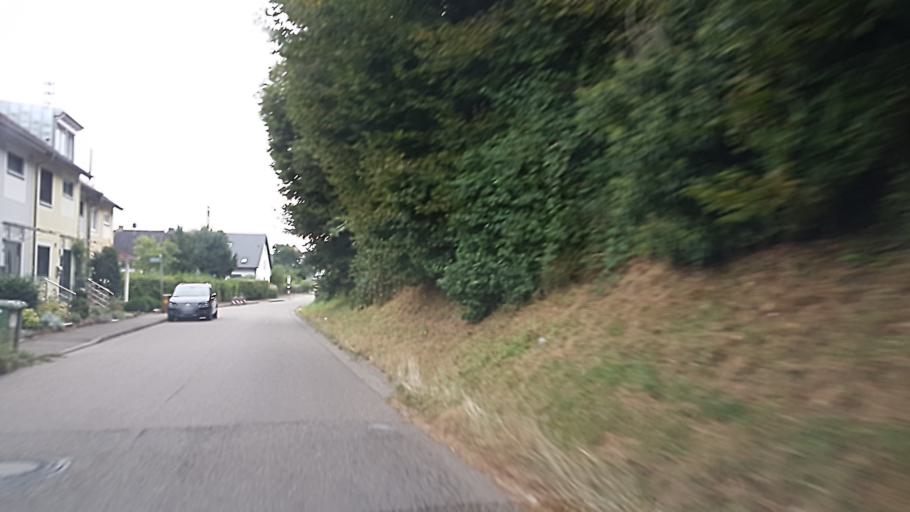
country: DE
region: Baden-Wuerttemberg
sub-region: Freiburg Region
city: Merdingen
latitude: 48.0054
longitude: 7.7207
